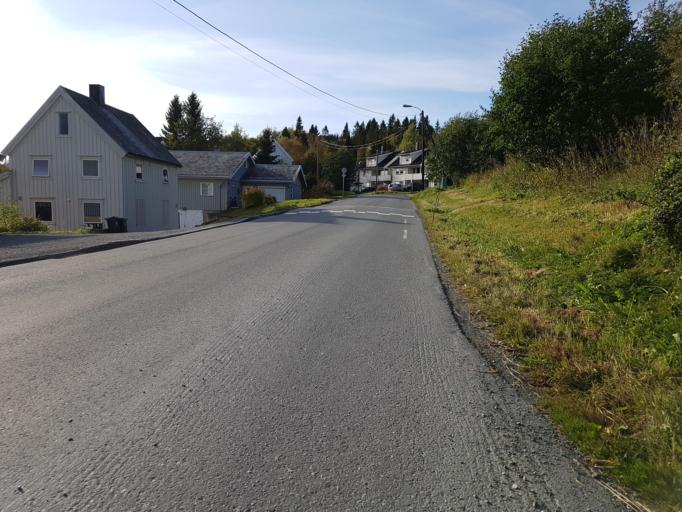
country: NO
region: Sor-Trondelag
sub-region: Klaebu
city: Klaebu
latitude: 63.3501
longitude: 10.4912
